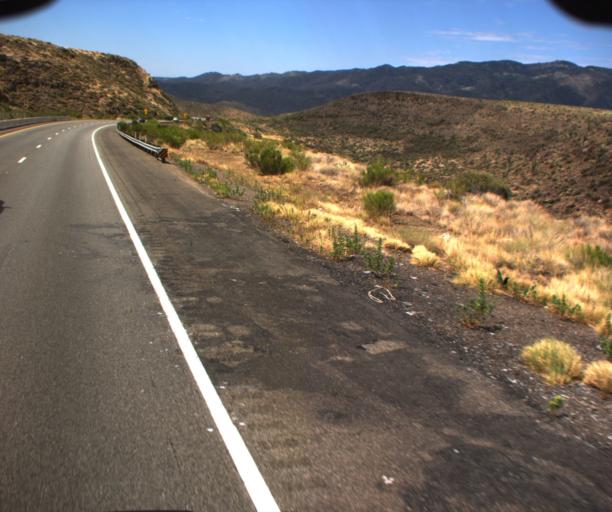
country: US
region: Arizona
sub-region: Yavapai County
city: Black Canyon City
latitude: 34.1679
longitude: -112.1433
